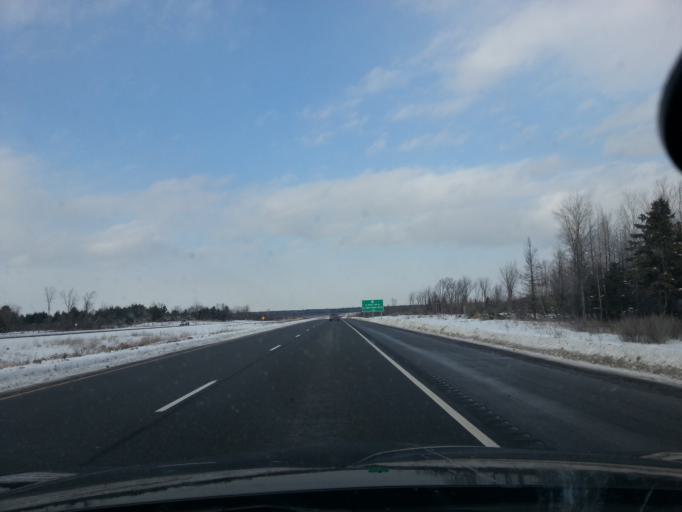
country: CA
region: Ontario
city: Carleton Place
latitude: 45.1881
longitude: -76.0453
